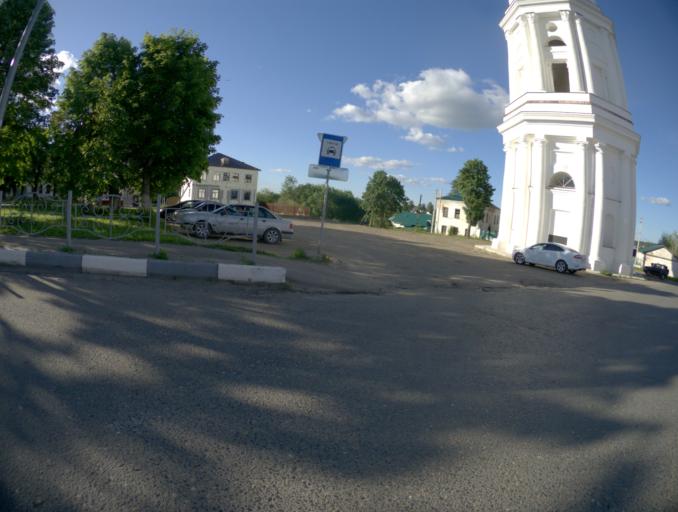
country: RU
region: Ivanovo
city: Lezhnevo
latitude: 56.7756
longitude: 40.8881
